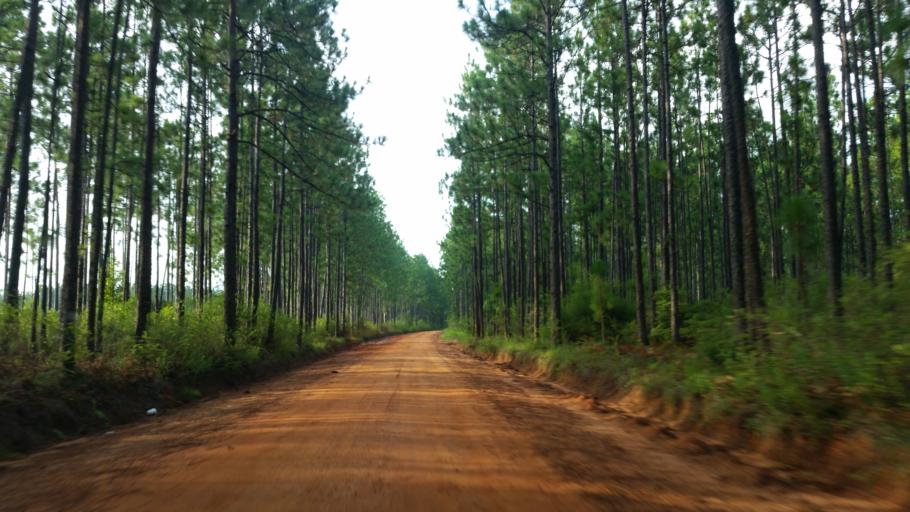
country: US
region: Alabama
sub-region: Escambia County
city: Atmore
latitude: 30.9489
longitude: -87.5721
